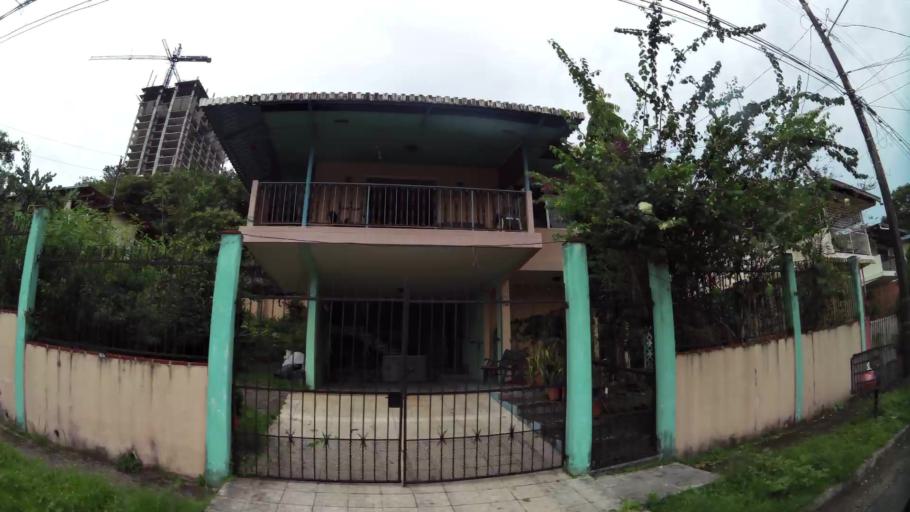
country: PA
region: Panama
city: Panama
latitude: 9.0255
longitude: -79.5177
